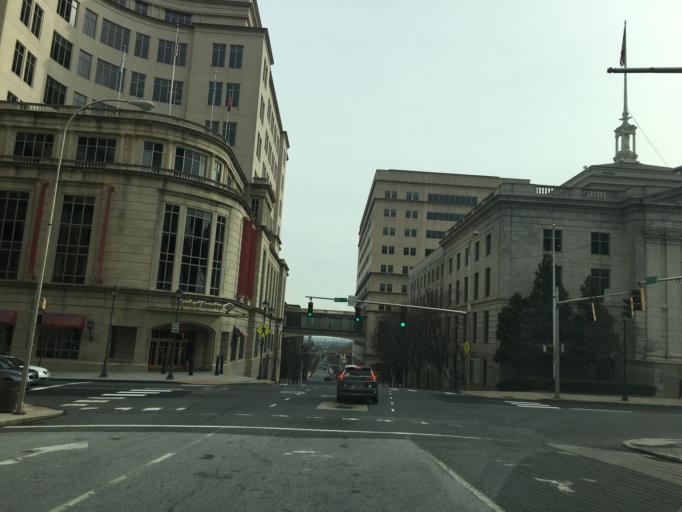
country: US
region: Delaware
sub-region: New Castle County
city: Wilmington
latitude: 39.7462
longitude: -75.5467
